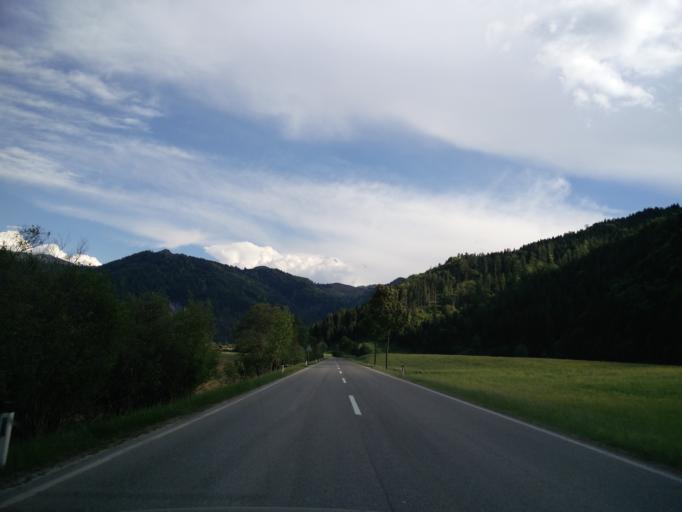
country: AT
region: Tyrol
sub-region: Politischer Bezirk Kitzbuhel
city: Kirchdorf in Tirol
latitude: 47.5899
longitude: 12.4702
